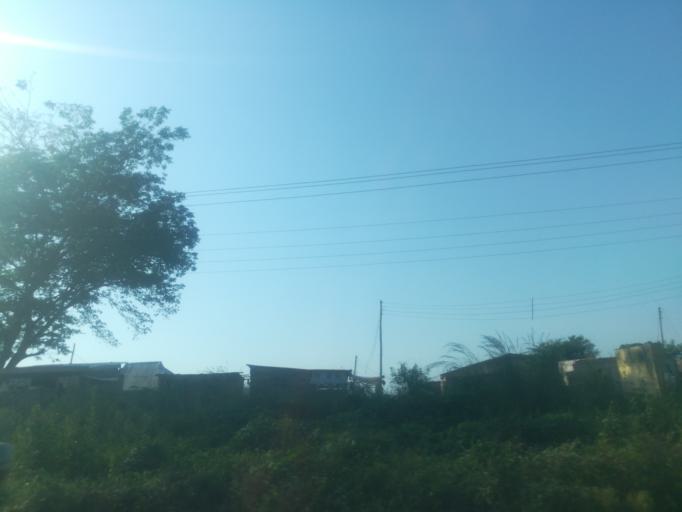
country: NG
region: Ogun
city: Abeokuta
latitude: 7.1696
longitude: 3.2718
